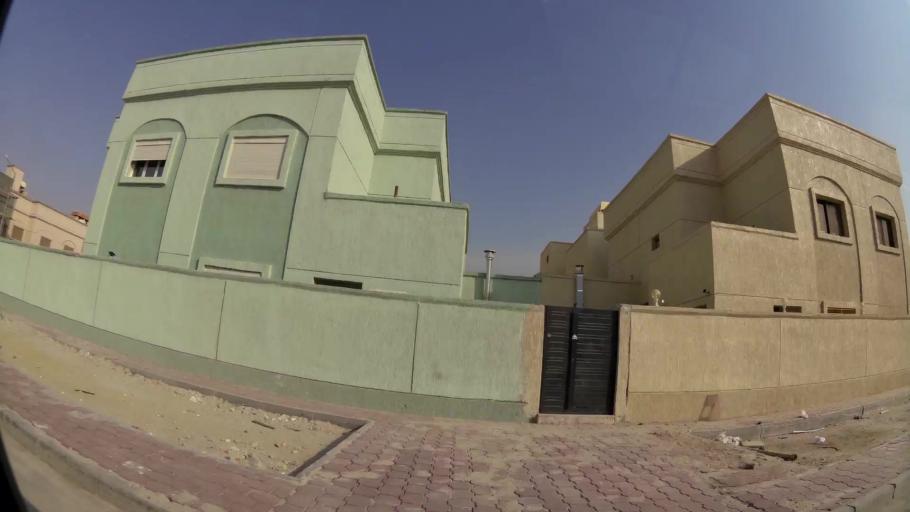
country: KW
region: Al Asimah
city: Ar Rabiyah
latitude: 29.3325
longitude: 47.8012
